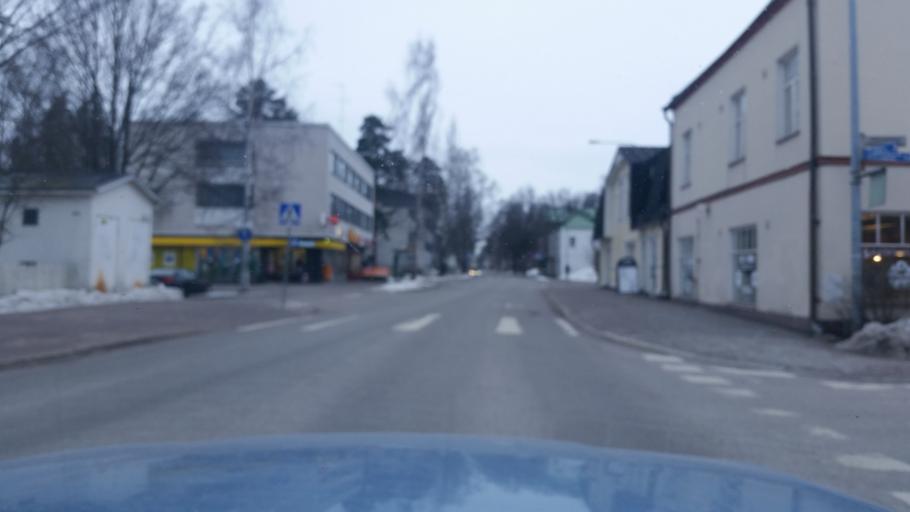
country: FI
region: Uusimaa
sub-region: Helsinki
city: Vantaa
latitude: 60.2625
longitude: 25.0272
